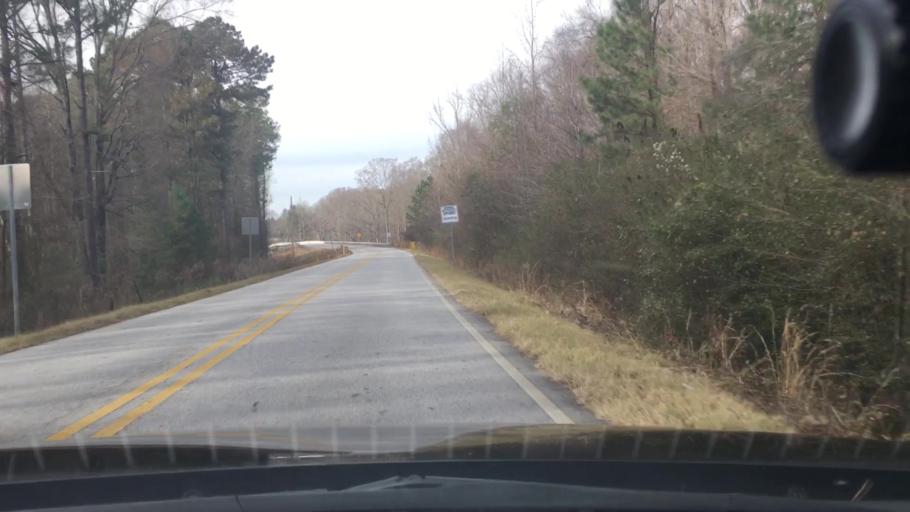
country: US
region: Georgia
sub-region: Fayette County
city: Shannon
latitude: 33.2802
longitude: -84.4222
